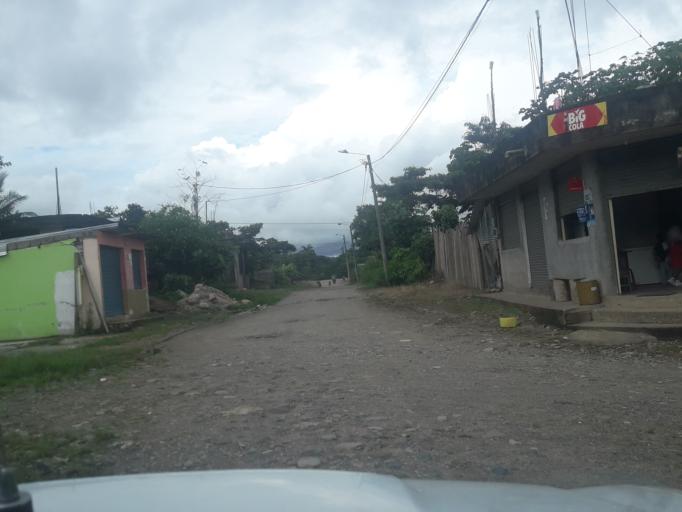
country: EC
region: Napo
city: Archidona
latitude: -0.9447
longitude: -77.8169
